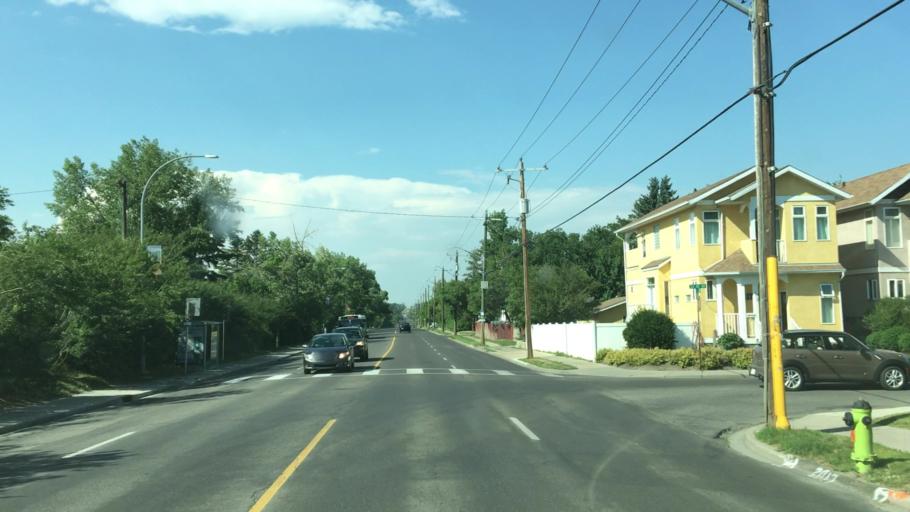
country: CA
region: Alberta
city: Calgary
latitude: 51.0814
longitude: -114.0715
